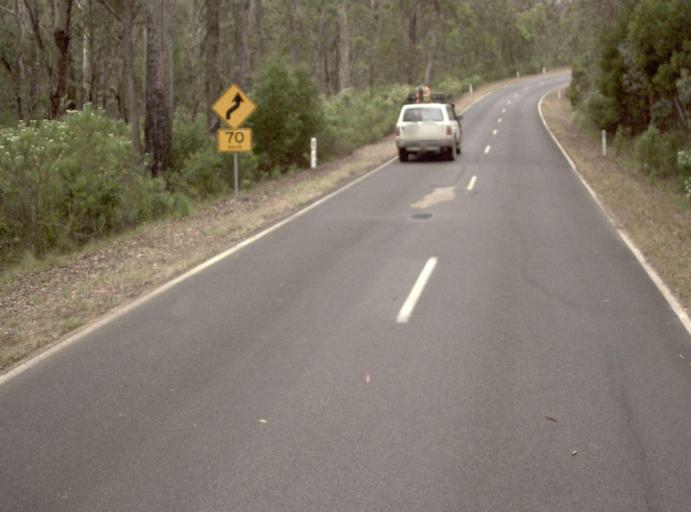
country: AU
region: Victoria
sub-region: East Gippsland
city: Bairnsdale
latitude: -37.6398
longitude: 147.2558
